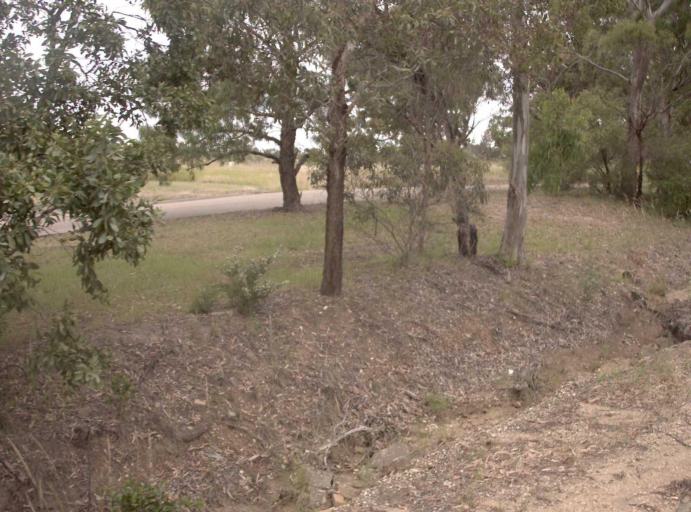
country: AU
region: Victoria
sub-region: East Gippsland
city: Bairnsdale
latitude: -37.8077
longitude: 147.6187
